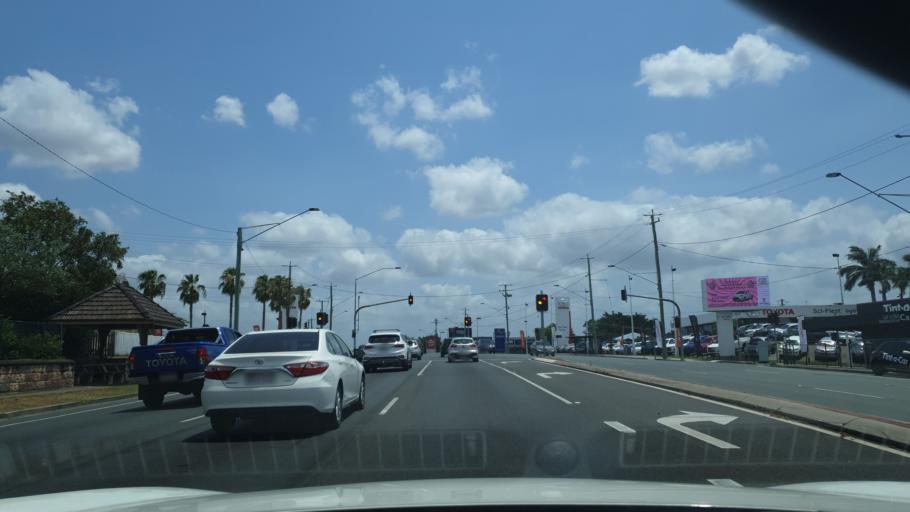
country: AU
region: Queensland
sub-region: Brisbane
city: Wavell Heights
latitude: -27.4005
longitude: 153.0315
